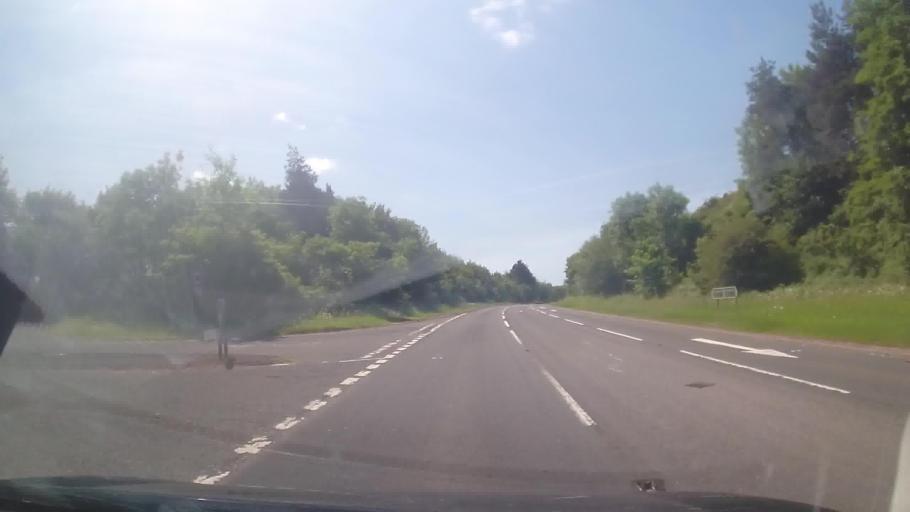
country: GB
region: England
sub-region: Herefordshire
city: Kimbolton
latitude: 52.3011
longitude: -2.6961
